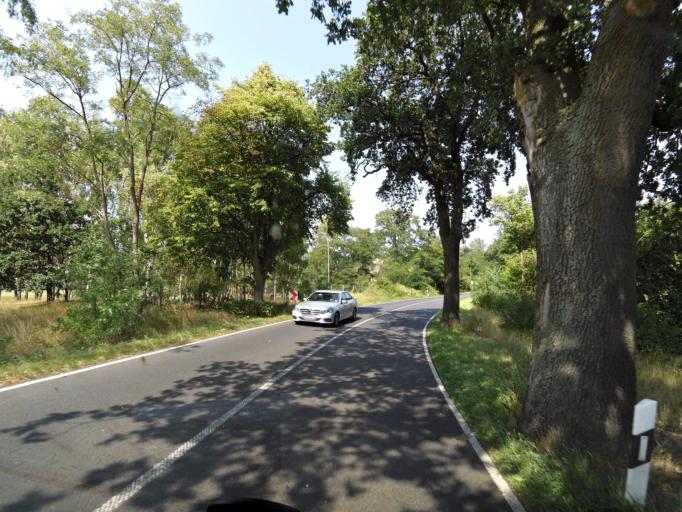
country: DE
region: Brandenburg
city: Liebenwalde
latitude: 52.8494
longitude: 13.3275
